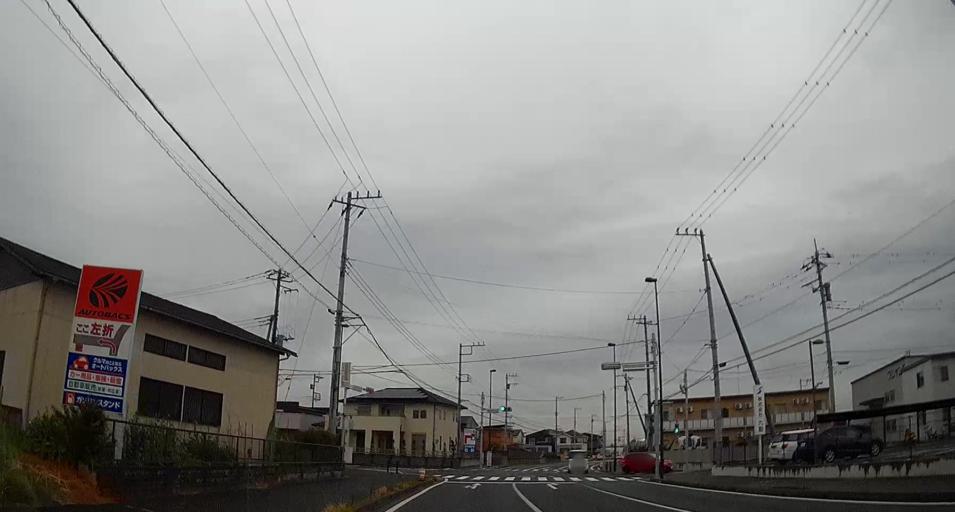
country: JP
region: Chiba
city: Kisarazu
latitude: 35.4289
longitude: 139.9353
